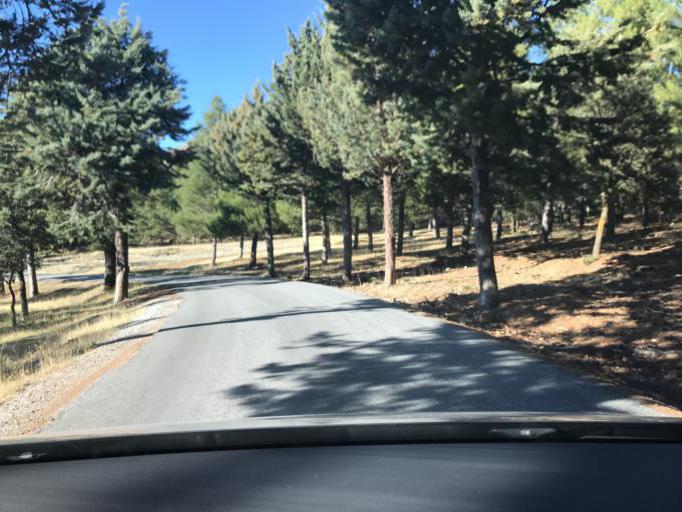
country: ES
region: Andalusia
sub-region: Provincia de Granada
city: Beas de Granada
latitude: 37.3051
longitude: -3.4524
